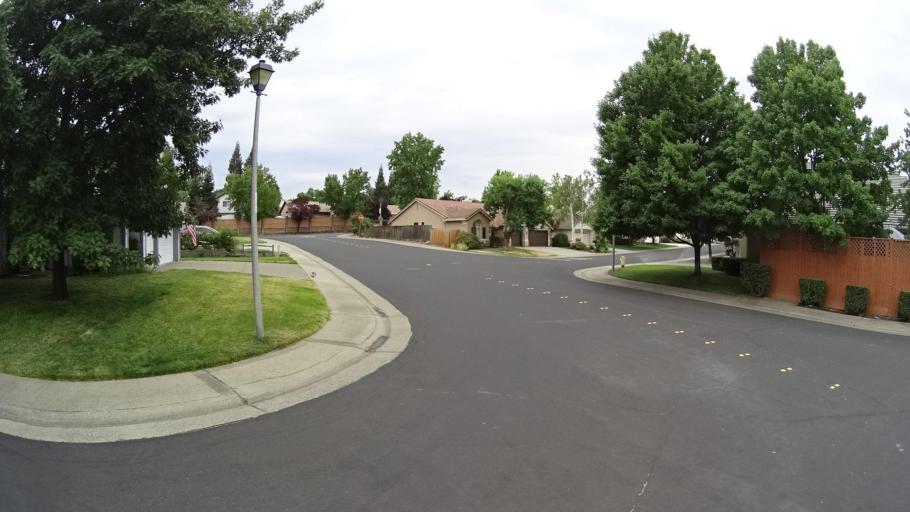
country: US
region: California
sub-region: Placer County
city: Rocklin
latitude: 38.7875
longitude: -121.2644
